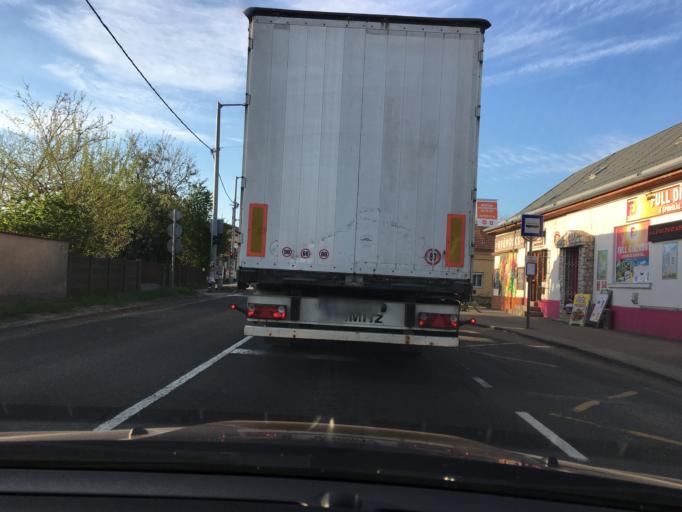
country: HU
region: Hajdu-Bihar
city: Mikepercs
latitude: 47.4392
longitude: 21.6314
